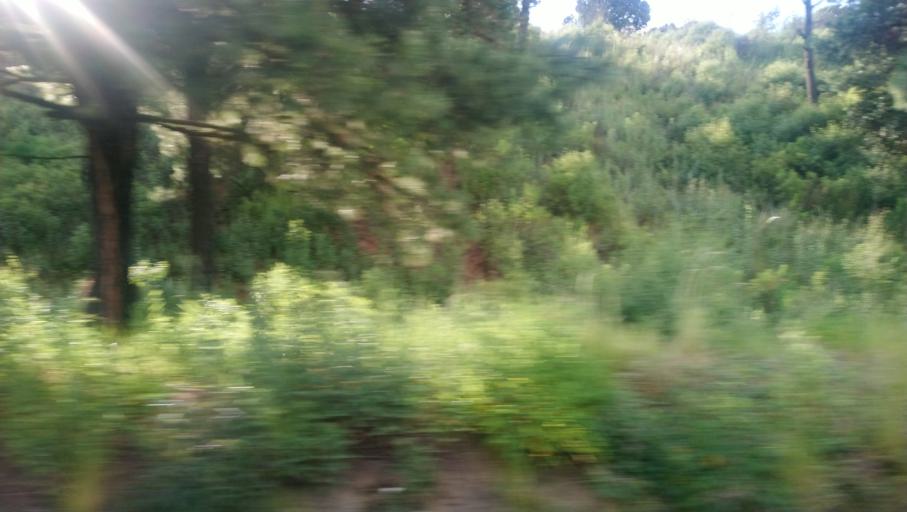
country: MX
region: Mexico
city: Juchitepec de Mariano Riva Palacio
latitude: 19.1315
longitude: -98.9360
